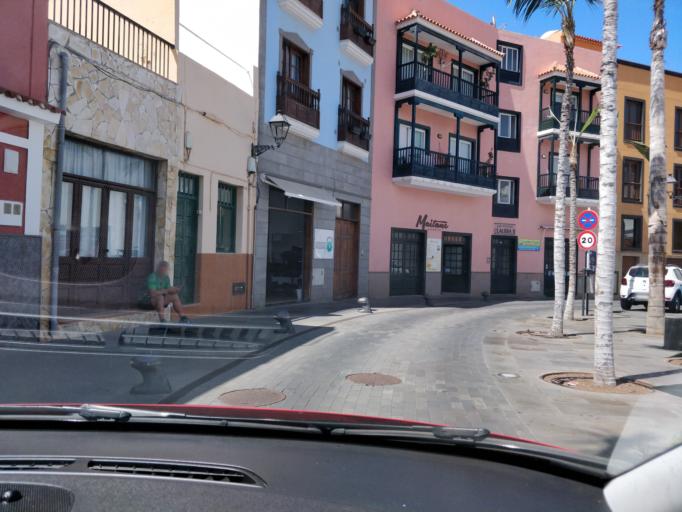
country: ES
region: Canary Islands
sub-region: Provincia de Santa Cruz de Tenerife
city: Puerto de la Cruz
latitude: 28.4174
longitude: -16.5547
